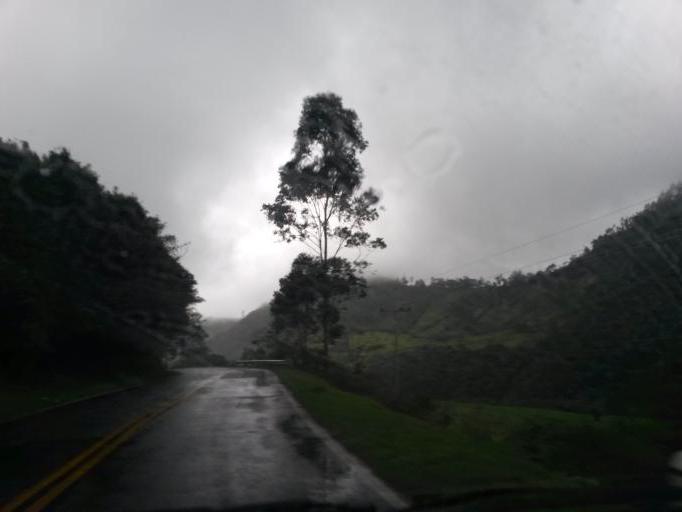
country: CO
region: Cauca
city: Popayan
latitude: 2.3643
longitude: -76.4935
